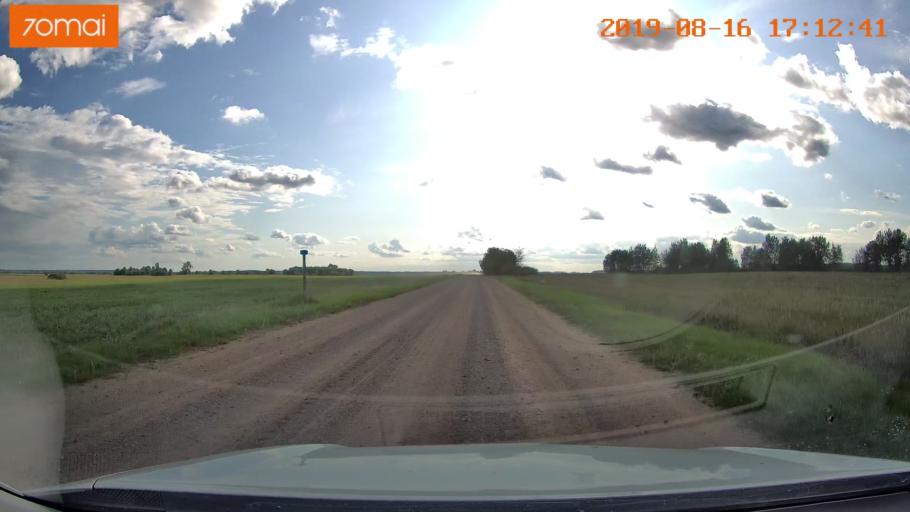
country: BY
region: Mogilev
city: Hlusha
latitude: 53.1939
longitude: 28.8884
